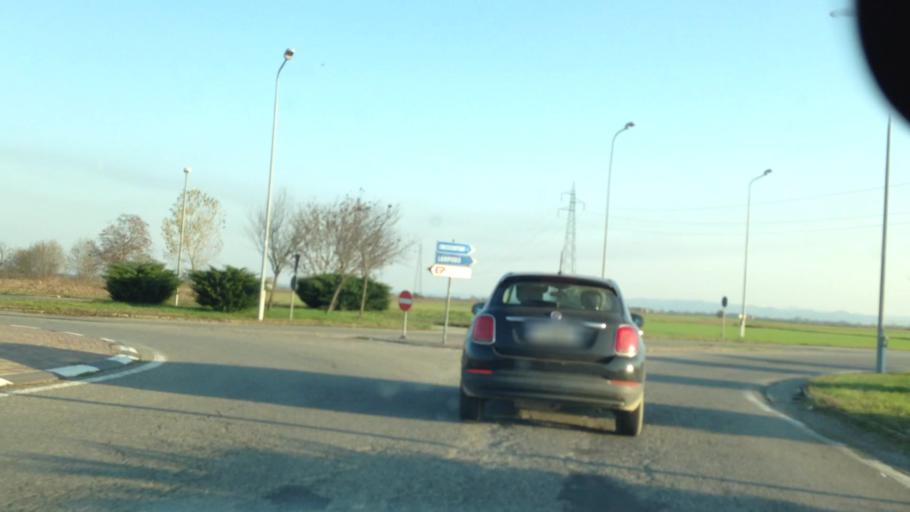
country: IT
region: Piedmont
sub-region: Provincia di Vercelli
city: Livorno Ferraris
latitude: 45.2724
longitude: 8.0811
